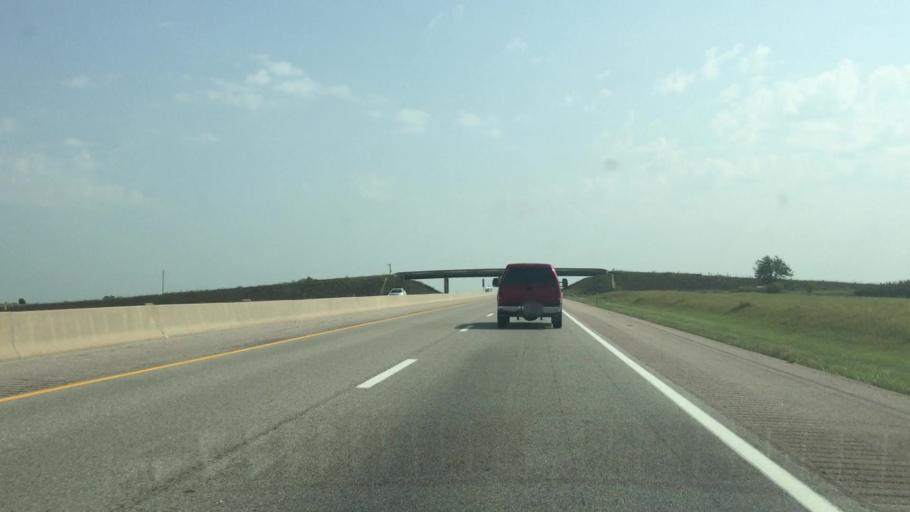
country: US
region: Kansas
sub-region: Butler County
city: El Dorado
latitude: 37.9966
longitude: -96.6943
